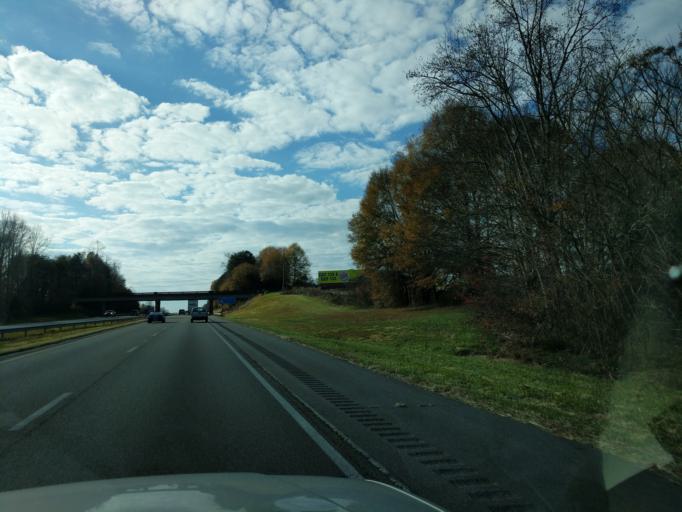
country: US
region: North Carolina
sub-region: Catawba County
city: Claremont
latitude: 35.7256
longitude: -81.1413
